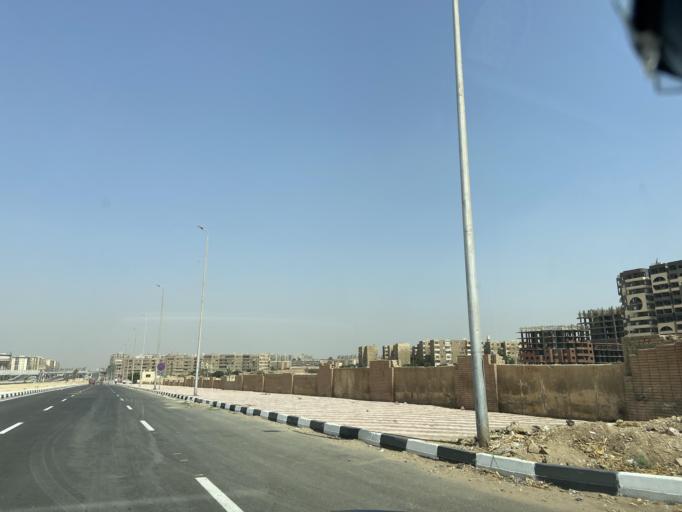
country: EG
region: Muhafazat al Qahirah
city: Cairo
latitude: 30.0394
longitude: 31.3590
